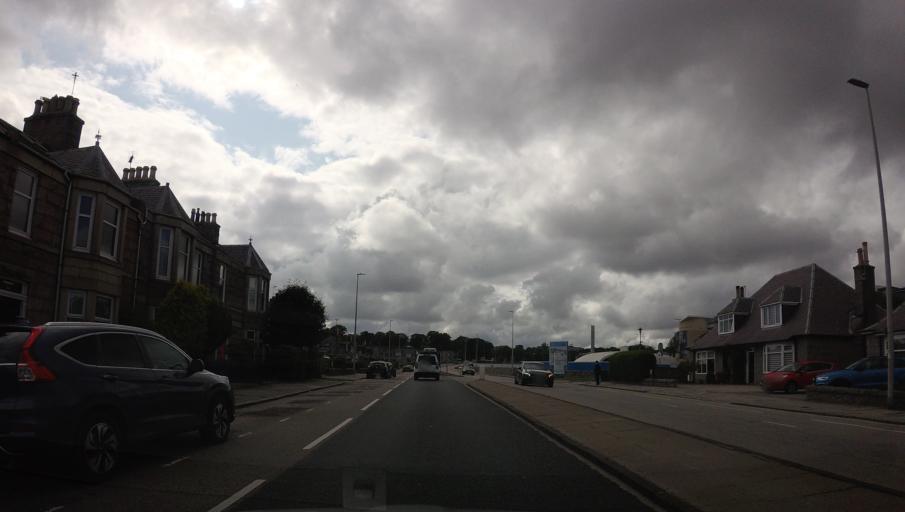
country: GB
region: Scotland
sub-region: Aberdeen City
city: Aberdeen
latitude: 57.1524
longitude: -2.1313
